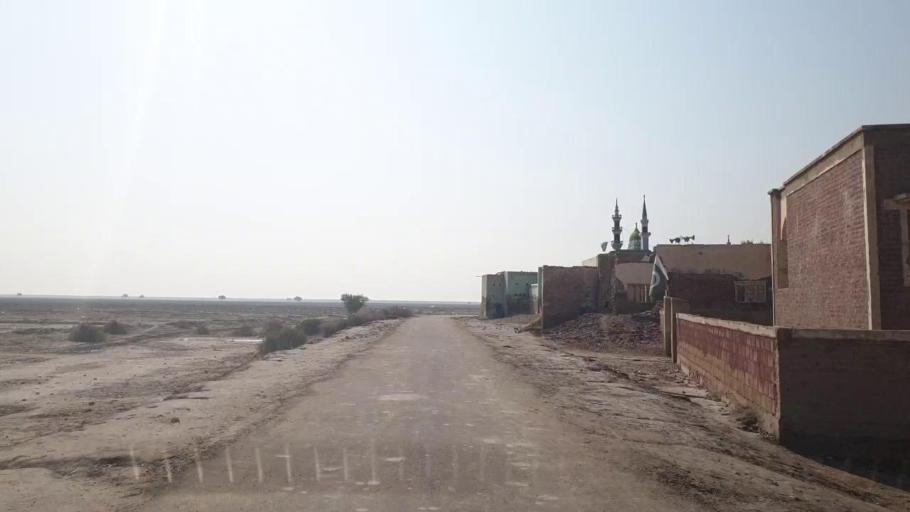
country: PK
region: Sindh
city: Bhan
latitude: 26.4357
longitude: 67.7354
